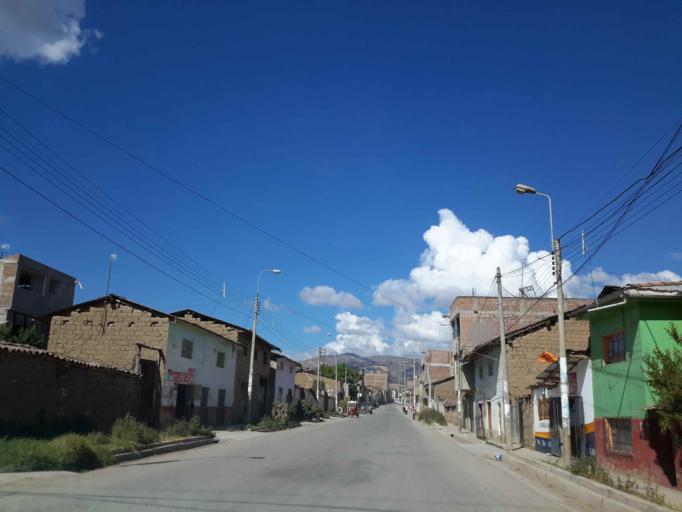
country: PE
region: Apurimac
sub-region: Provincia de Andahuaylas
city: Talavera
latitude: -13.6525
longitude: -73.4339
